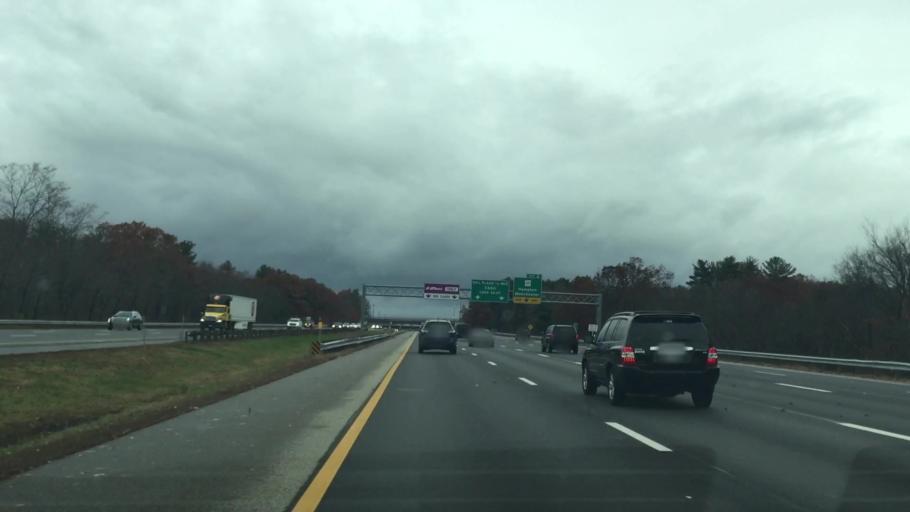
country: US
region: New Hampshire
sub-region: Rockingham County
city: Hampton
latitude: 42.9499
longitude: -70.8588
